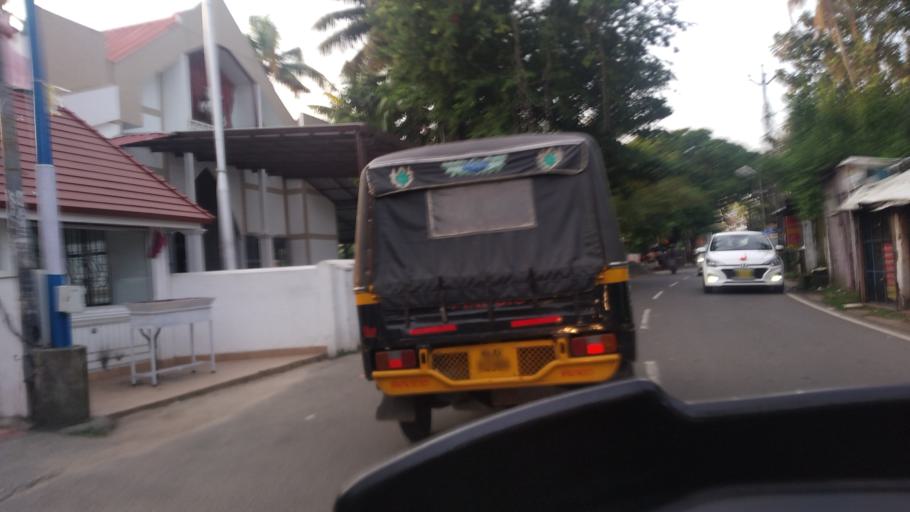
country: IN
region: Kerala
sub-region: Ernakulam
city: Elur
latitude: 10.0140
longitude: 76.2858
